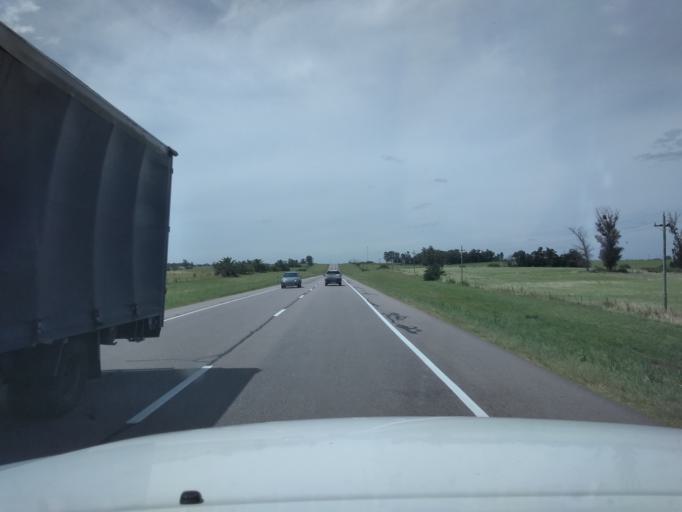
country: UY
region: Florida
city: Florida
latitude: -34.2208
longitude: -56.2090
